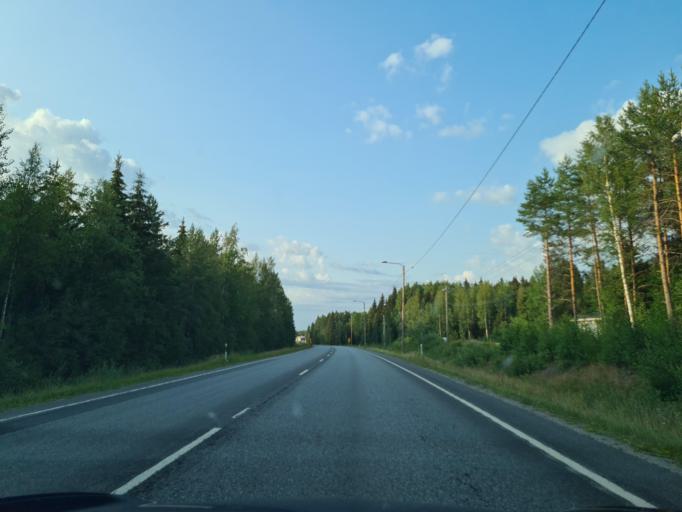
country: FI
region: Southern Ostrobothnia
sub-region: Seinaejoki
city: Kauhava
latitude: 63.0750
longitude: 23.0556
